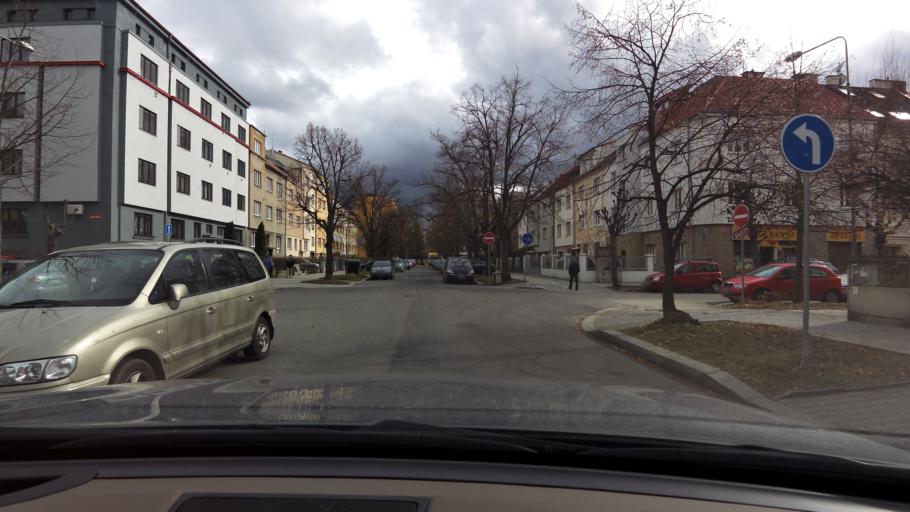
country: CZ
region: Plzensky
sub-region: Okres Plzen-Mesto
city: Pilsen
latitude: 49.7266
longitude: 13.3710
